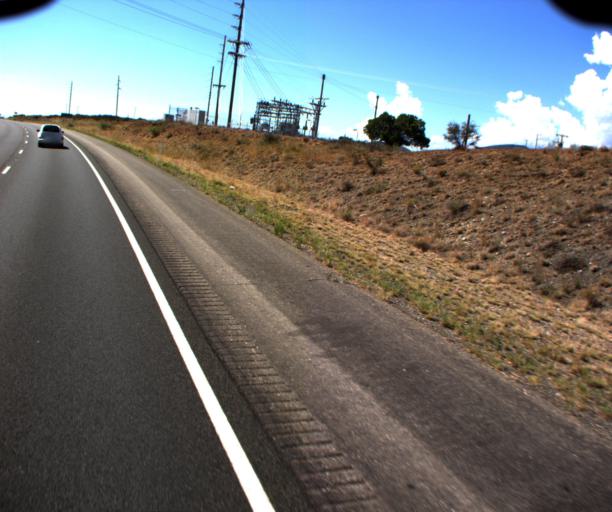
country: US
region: Arizona
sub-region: Yavapai County
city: Mayer
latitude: 34.4536
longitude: -112.2718
